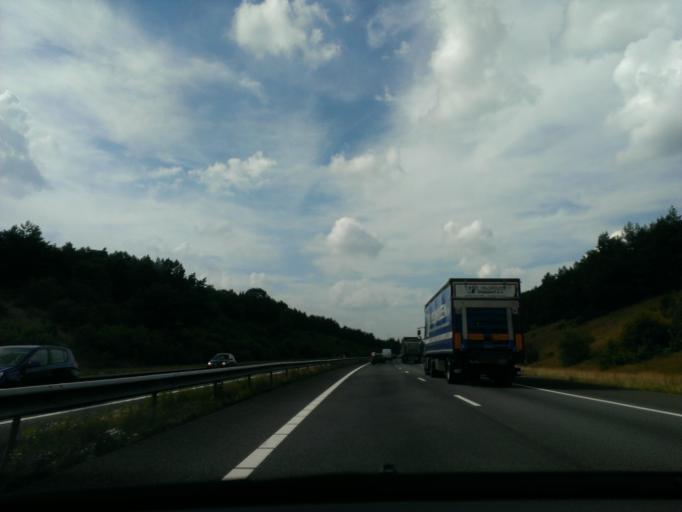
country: NL
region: Gelderland
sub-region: Gemeente Apeldoorn
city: Uddel
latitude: 52.1914
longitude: 5.8431
